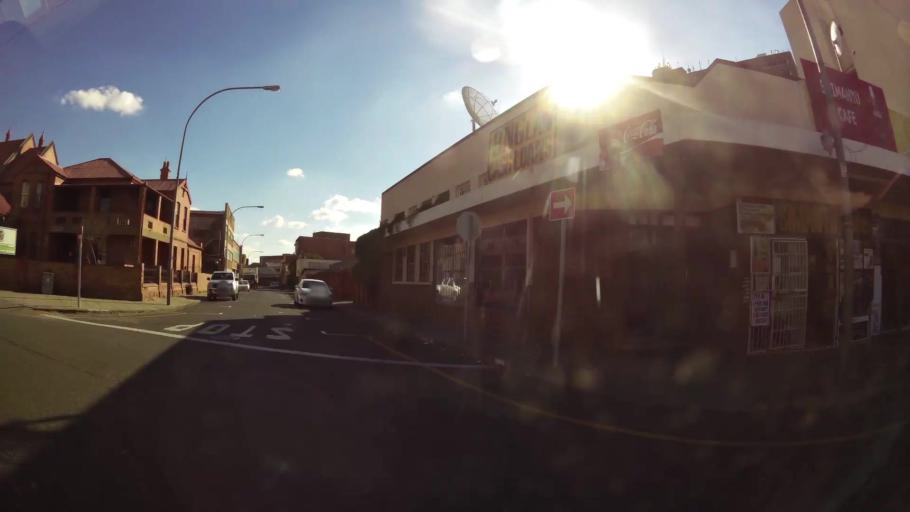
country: ZA
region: Northern Cape
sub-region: Frances Baard District Municipality
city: Kimberley
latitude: -28.7390
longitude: 24.7658
